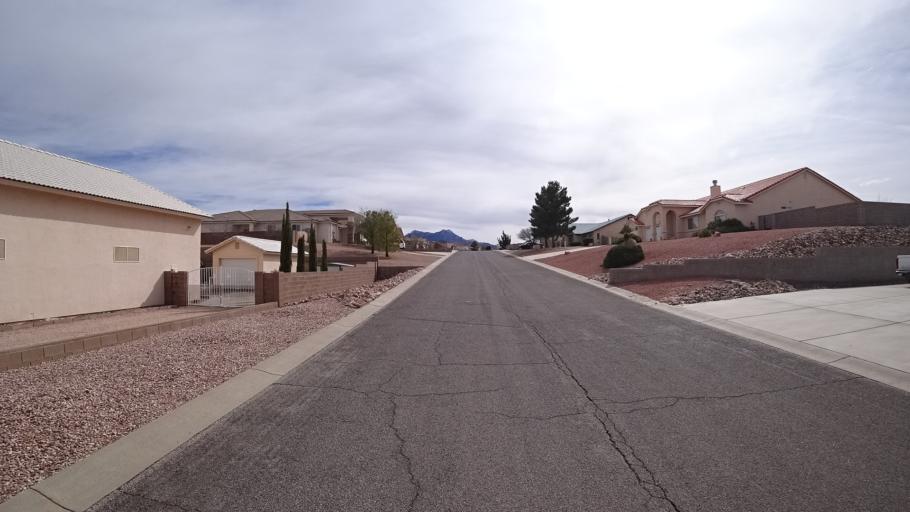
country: US
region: Arizona
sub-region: Mohave County
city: Kingman
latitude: 35.1917
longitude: -113.9803
